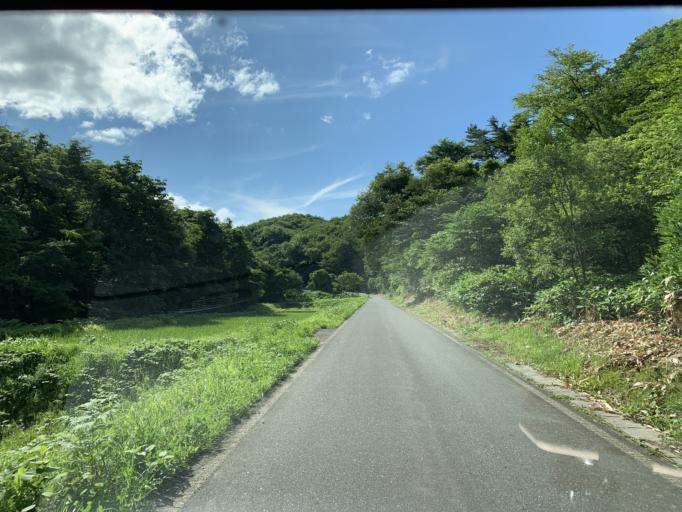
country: JP
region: Iwate
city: Ichinoseki
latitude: 38.9204
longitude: 140.9683
